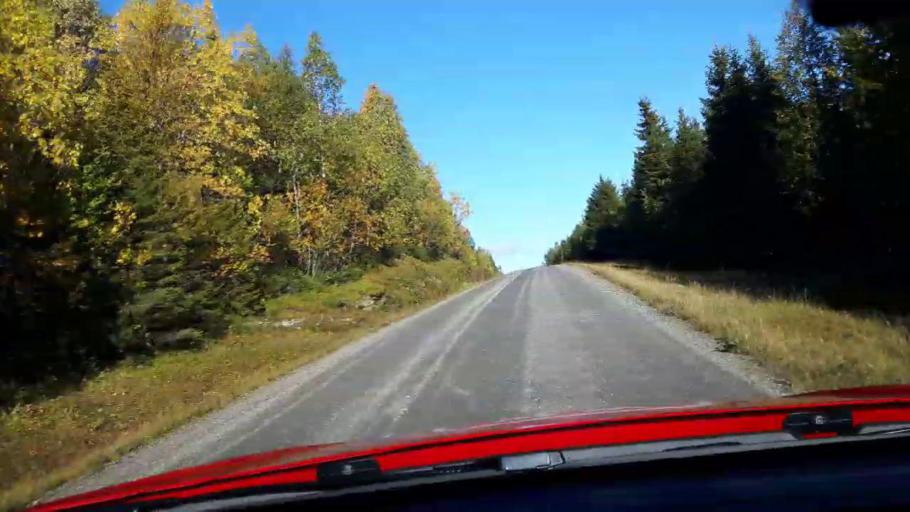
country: NO
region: Nord-Trondelag
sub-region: Lierne
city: Sandvika
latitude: 64.5802
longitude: 13.8914
